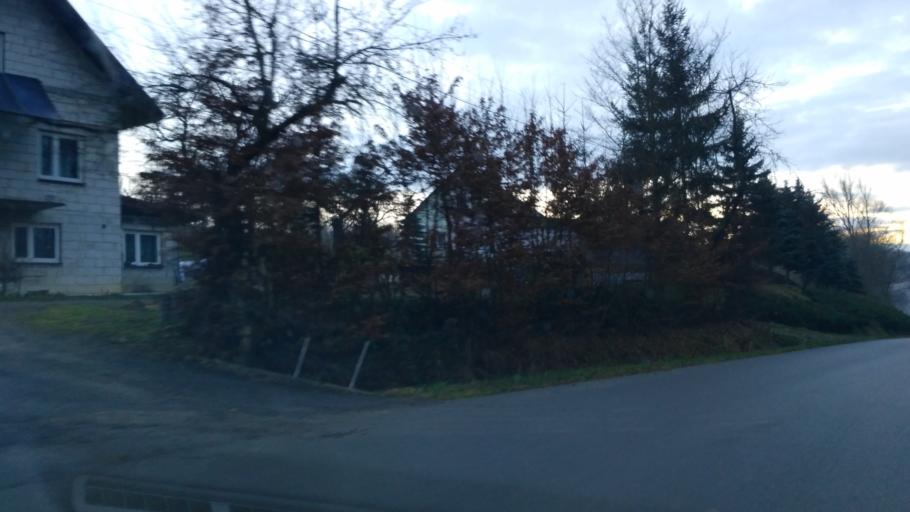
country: PL
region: Subcarpathian Voivodeship
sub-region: Powiat strzyzowski
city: Niebylec
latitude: 49.8719
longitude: 21.8778
